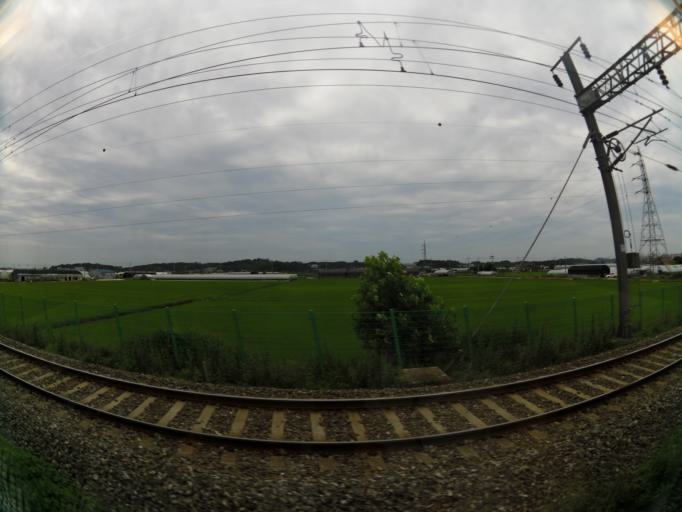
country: KR
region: Gyeonggi-do
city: Osan
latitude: 37.1179
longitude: 127.0633
